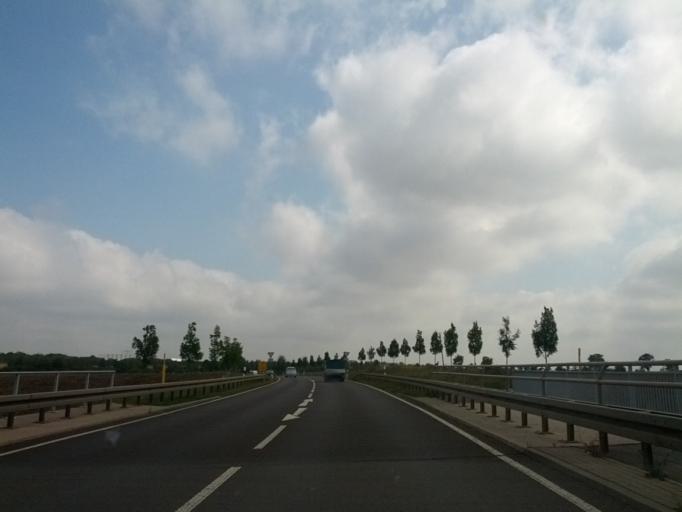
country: DE
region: Thuringia
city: Emleben
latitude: 50.9235
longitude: 10.6961
